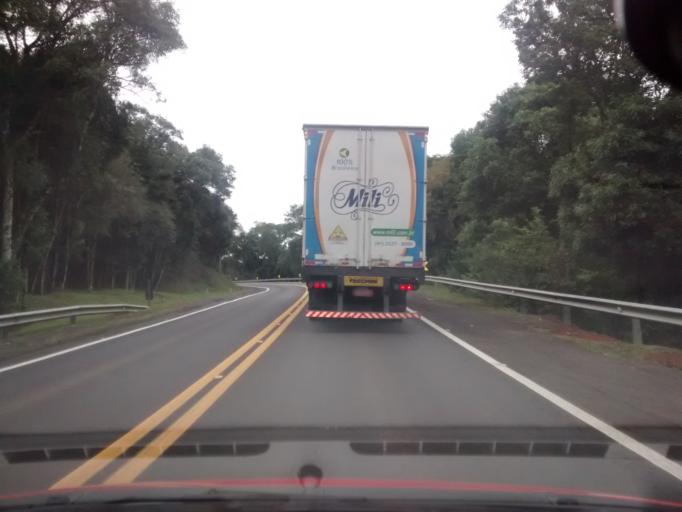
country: BR
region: Rio Grande do Sul
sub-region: Vacaria
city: Estrela
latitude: -28.1967
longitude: -50.7348
